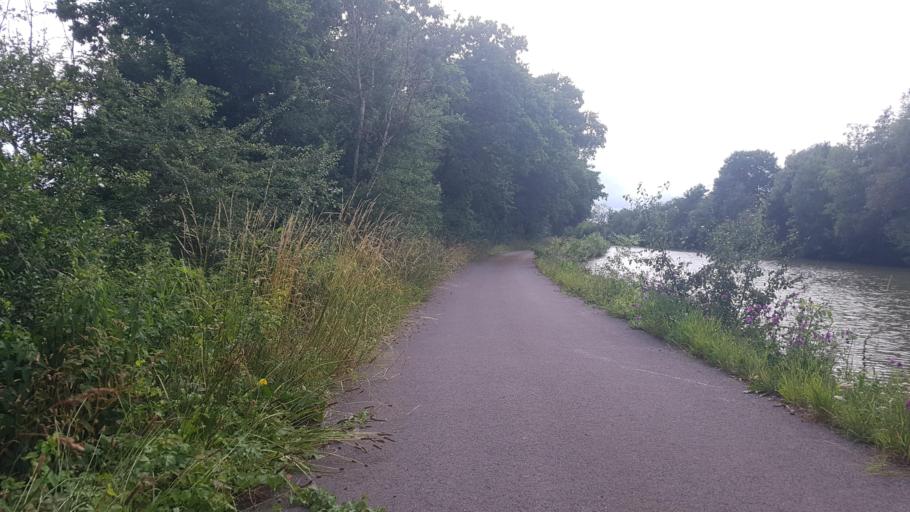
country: FR
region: Lorraine
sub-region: Departement de la Moselle
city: Dieuze
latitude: 48.6911
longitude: 6.7206
